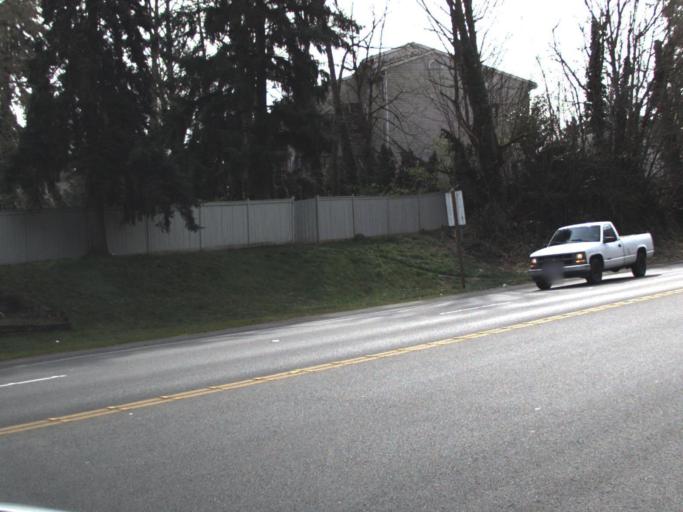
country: US
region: Washington
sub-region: King County
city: Normandy Park
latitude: 47.4466
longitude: -122.3339
